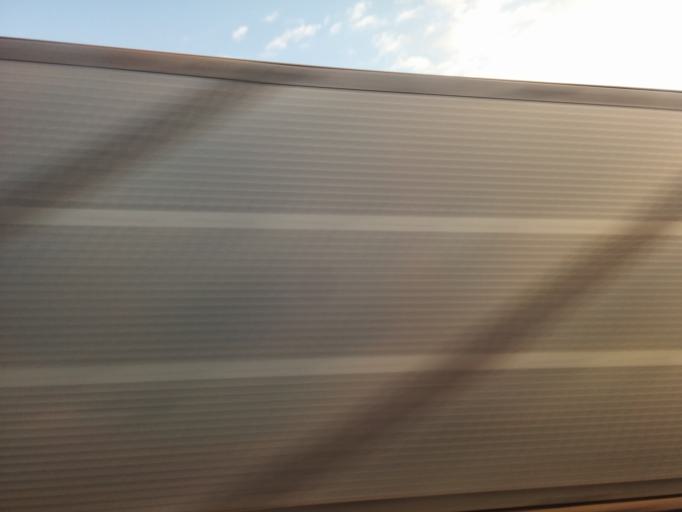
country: JP
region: Aichi
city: Chiryu
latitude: 34.9989
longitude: 137.0250
